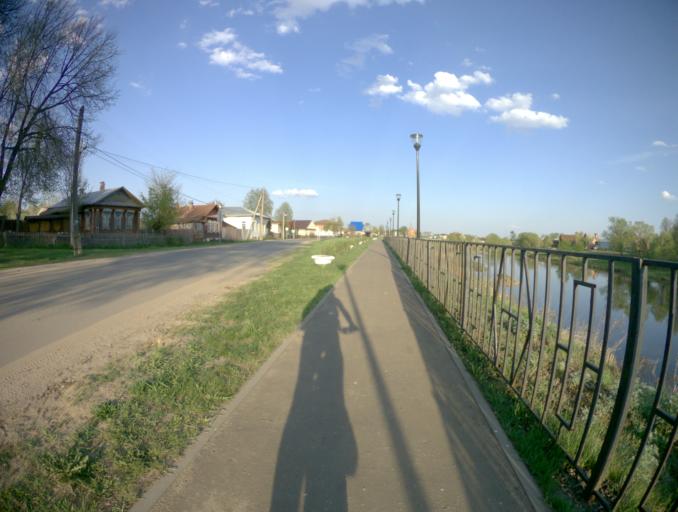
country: RU
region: Ivanovo
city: Yuzha
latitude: 56.5784
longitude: 41.8726
